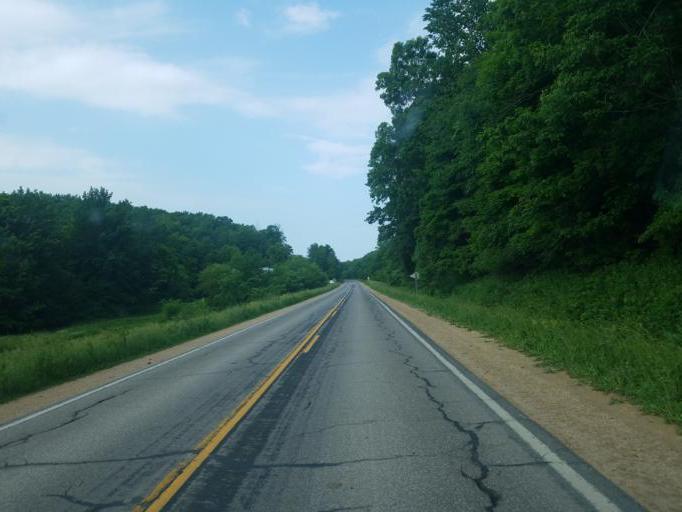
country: US
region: Wisconsin
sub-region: Vernon County
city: Hillsboro
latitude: 43.6383
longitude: -90.4433
